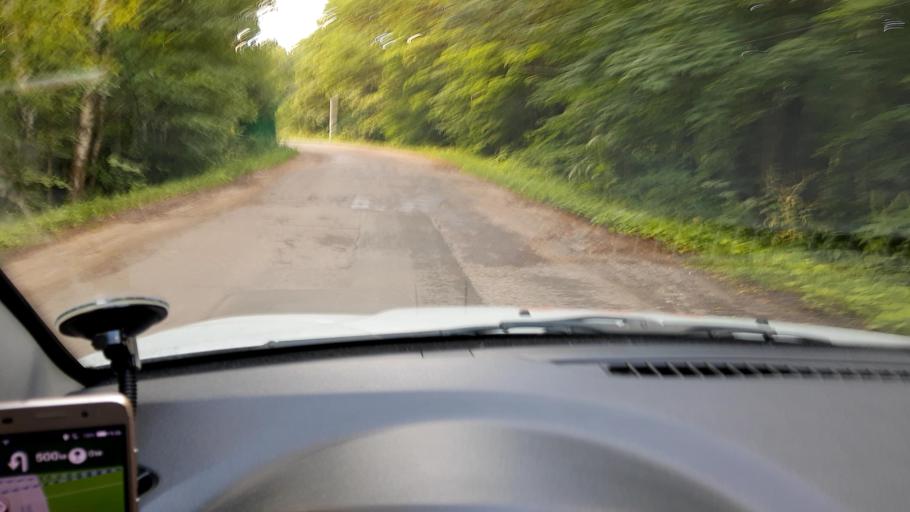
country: RU
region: Nizjnij Novgorod
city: Afonino
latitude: 56.2017
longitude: 44.0251
